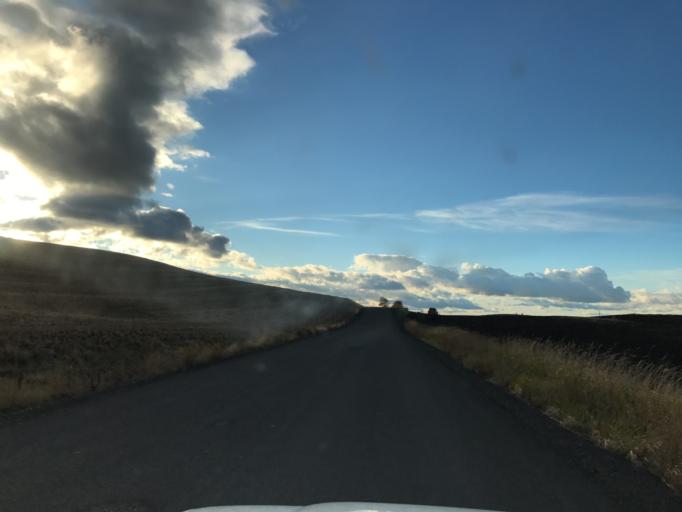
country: US
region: Idaho
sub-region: Latah County
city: Moscow
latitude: 46.7657
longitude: -116.9960
